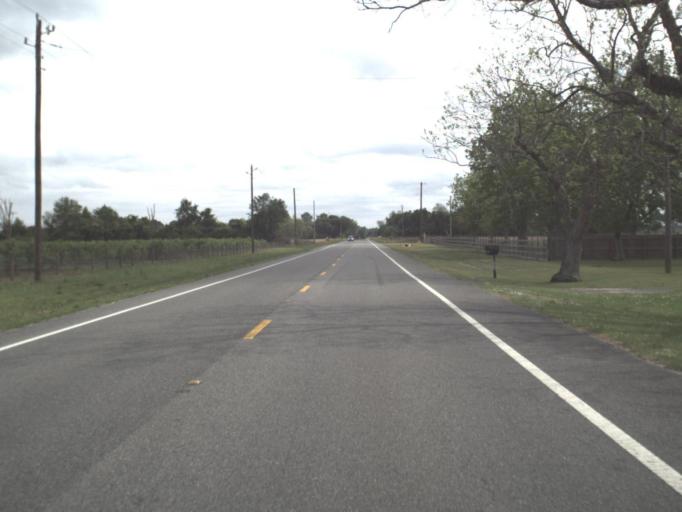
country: US
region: Florida
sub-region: Santa Rosa County
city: Point Baker
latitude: 30.7509
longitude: -87.0933
